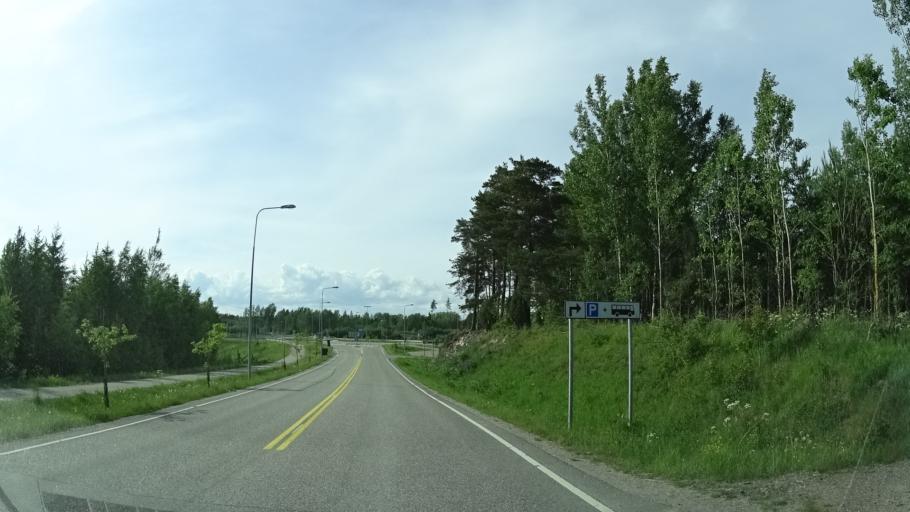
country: FI
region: Uusimaa
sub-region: Helsinki
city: Kirkkonummi
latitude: 60.1175
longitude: 24.4818
